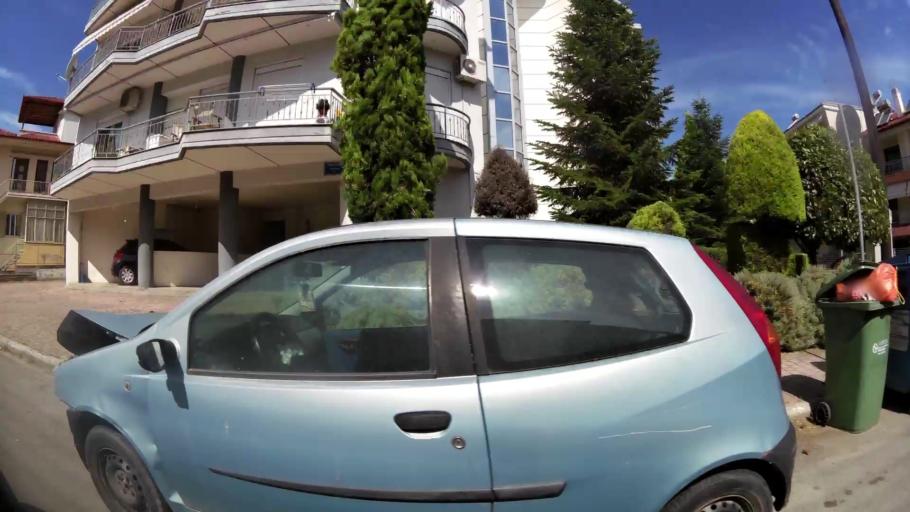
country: GR
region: Central Macedonia
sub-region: Nomos Pierias
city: Katerini
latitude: 40.2789
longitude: 22.5061
